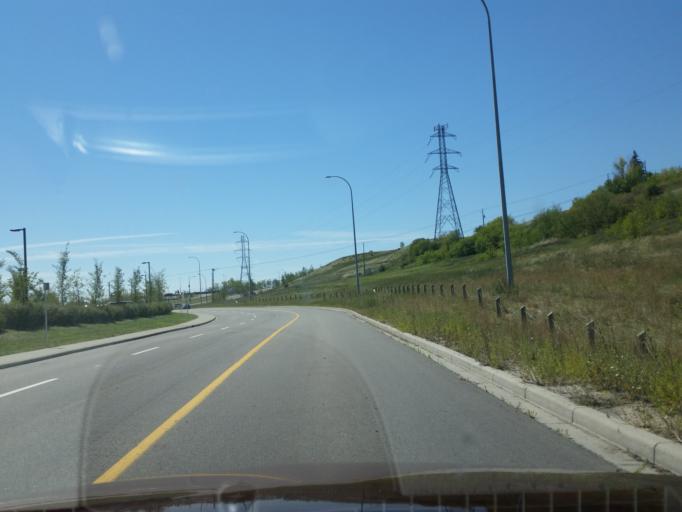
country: CA
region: Alberta
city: Calgary
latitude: 51.0547
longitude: -114.0266
